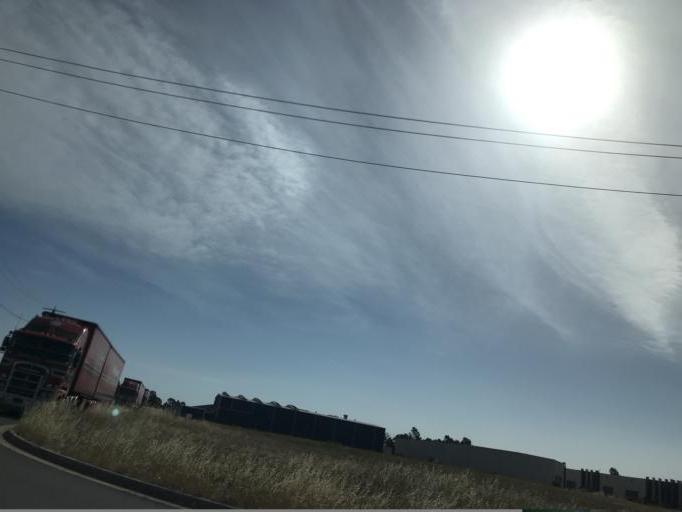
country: AU
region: Victoria
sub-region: Ballarat North
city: Newington
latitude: -37.5364
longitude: 143.8158
